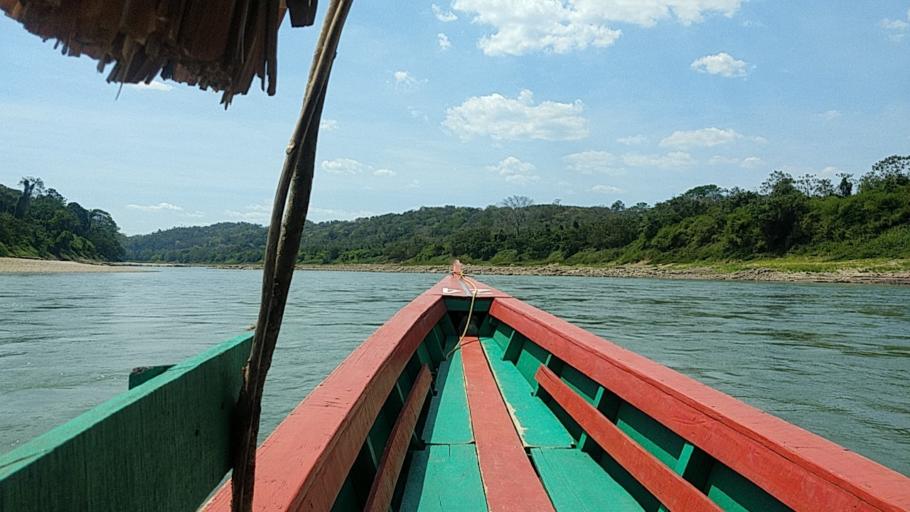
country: MX
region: Chiapas
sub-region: Ocosingo
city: Frontera Corozal
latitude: 16.8960
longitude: -90.9569
